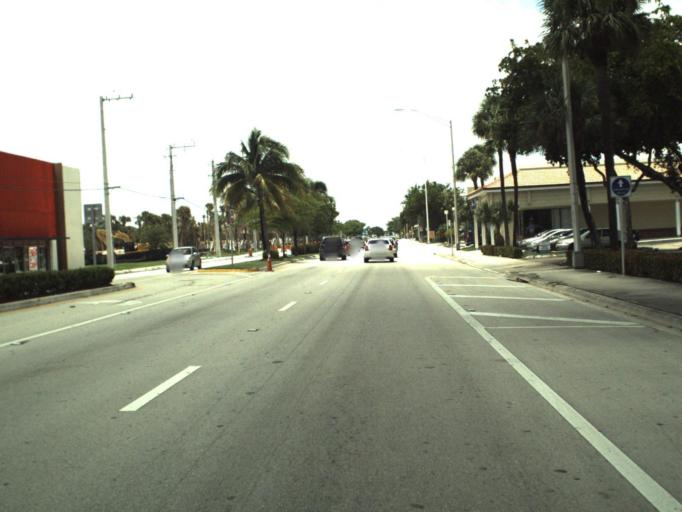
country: US
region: Florida
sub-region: Broward County
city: Pompano Beach
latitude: 26.2317
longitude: -80.1172
